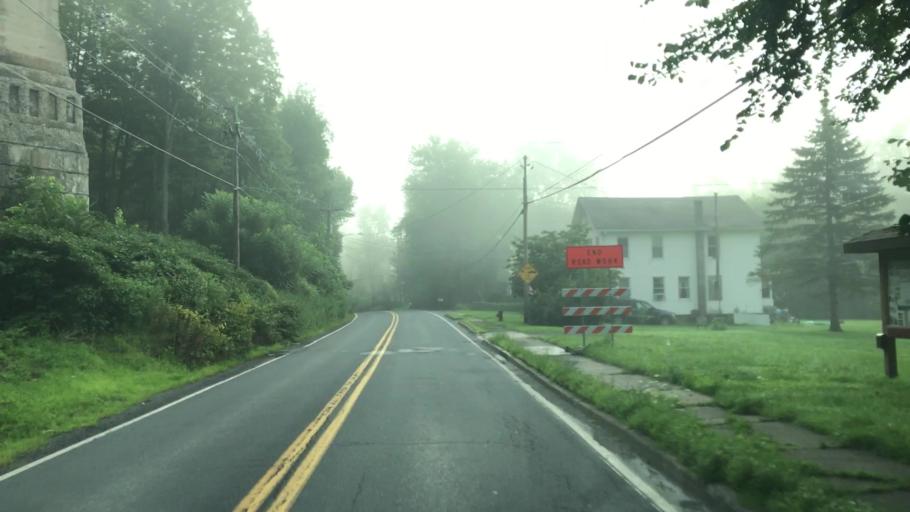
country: US
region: Pennsylvania
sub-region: Wyoming County
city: Factoryville
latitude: 41.6262
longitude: -75.7765
